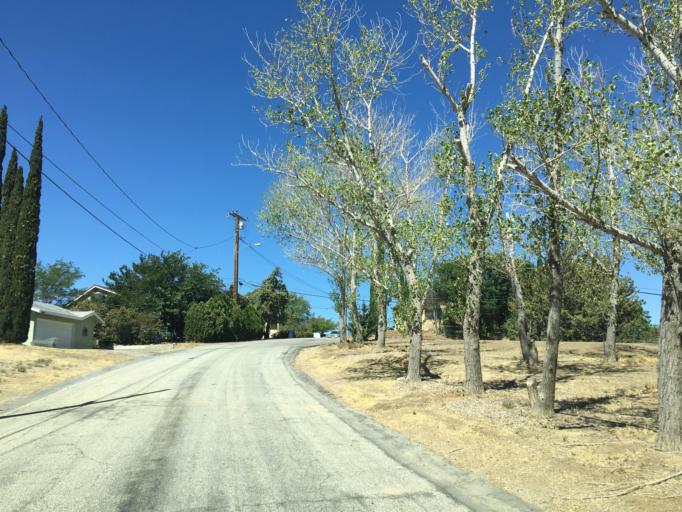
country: US
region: California
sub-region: Los Angeles County
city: Green Valley
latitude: 34.6554
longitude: -118.3798
